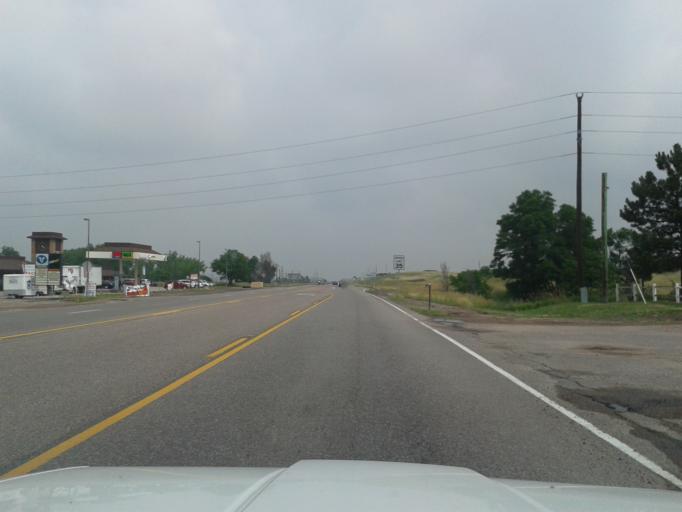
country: US
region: Colorado
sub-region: Douglas County
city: The Pinery
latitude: 39.3929
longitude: -104.7533
